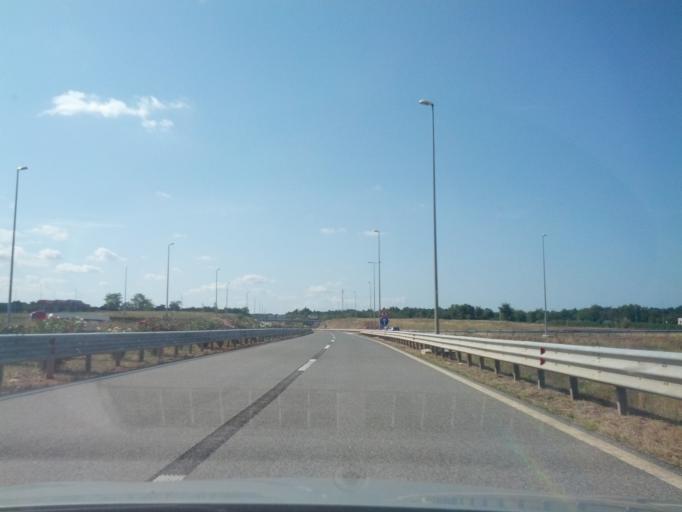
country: HR
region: Istarska
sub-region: Grad Porec
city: Porec
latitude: 45.2180
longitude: 13.7226
